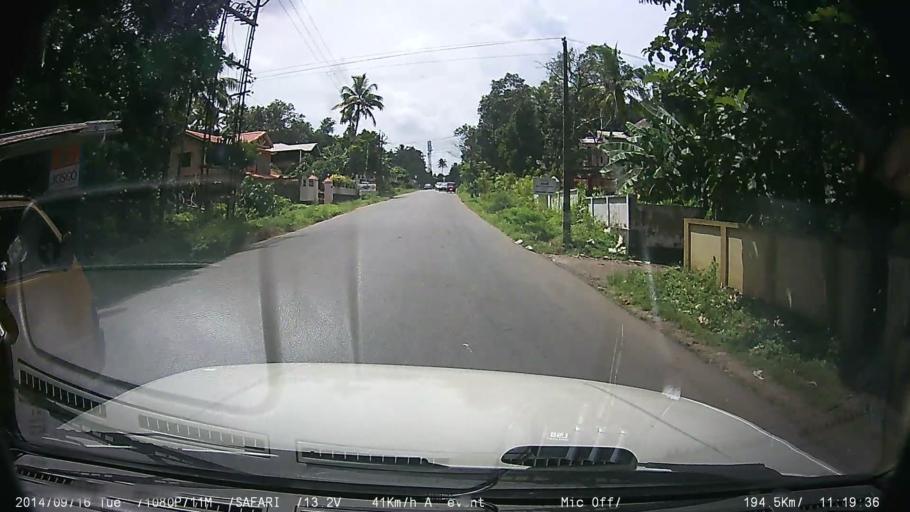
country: IN
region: Kerala
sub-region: Kottayam
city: Changanacheri
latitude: 9.4905
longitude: 76.5247
